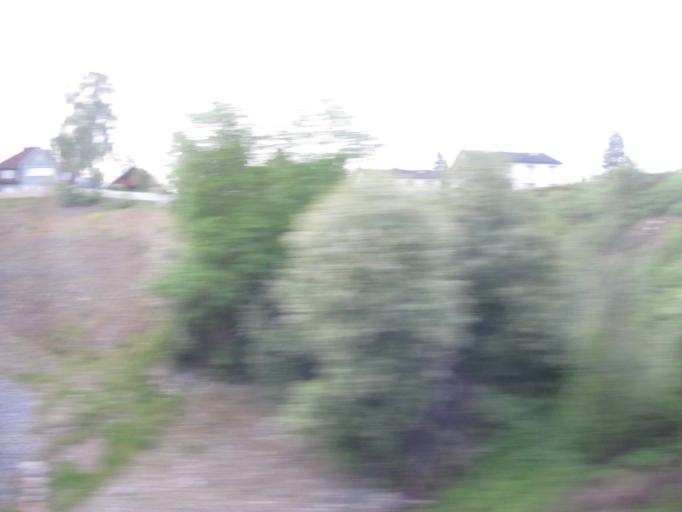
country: NO
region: Oppland
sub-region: Lillehammer
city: Lillehammer
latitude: 61.1060
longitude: 10.4646
